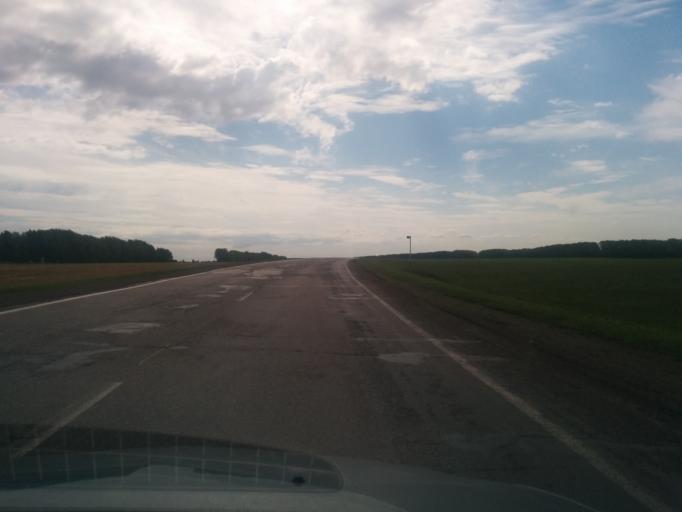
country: RU
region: Bashkortostan
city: Kabakovo
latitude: 54.4638
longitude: 55.9610
